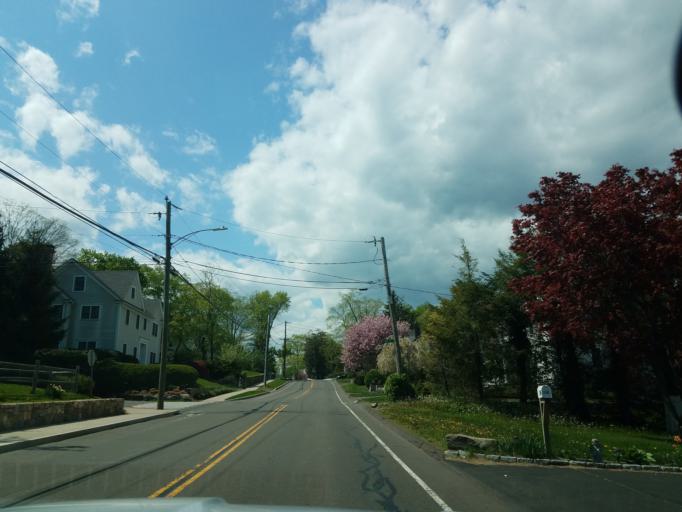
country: US
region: Connecticut
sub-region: Fairfield County
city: New Canaan
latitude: 41.1428
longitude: -73.4865
